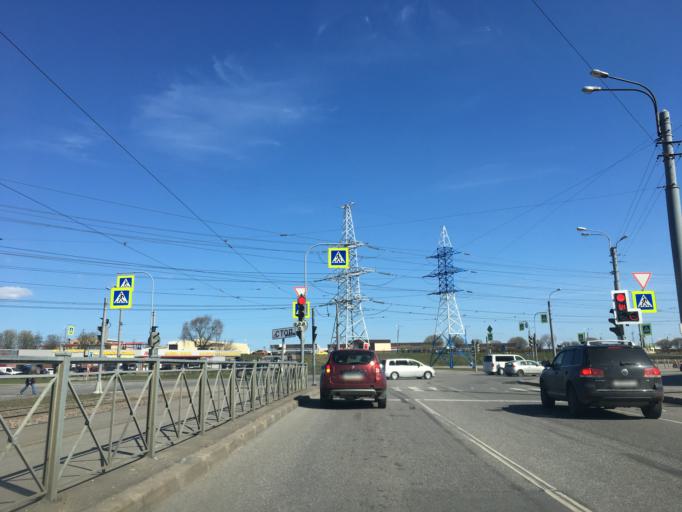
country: RU
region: St.-Petersburg
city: Uritsk
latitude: 59.8596
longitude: 30.2059
